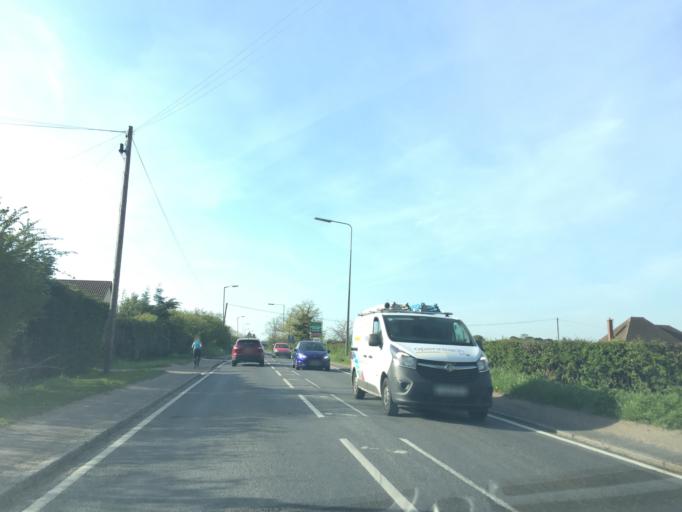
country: GB
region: England
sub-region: Essex
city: Epping
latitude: 51.7237
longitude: 0.1270
